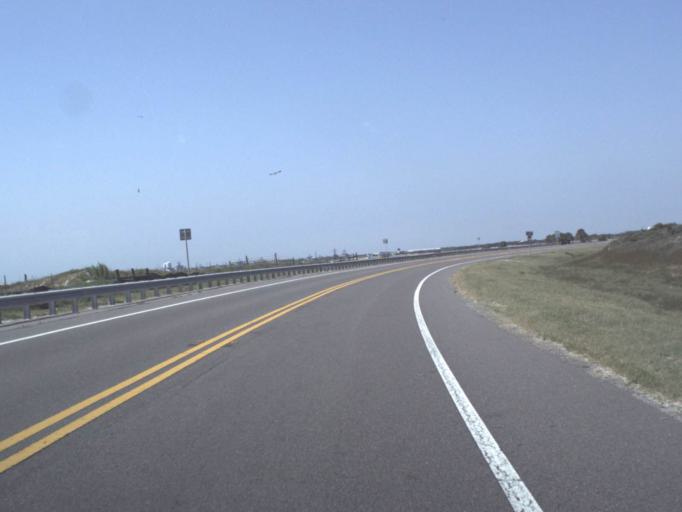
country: US
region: Florida
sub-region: Duval County
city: Atlantic Beach
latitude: 30.4263
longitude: -81.4112
